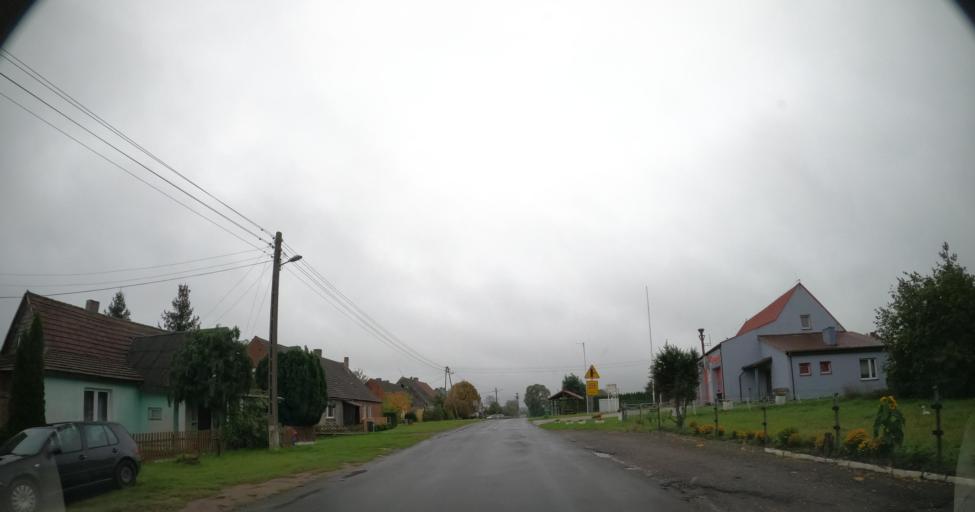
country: PL
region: West Pomeranian Voivodeship
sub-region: Powiat pyrzycki
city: Kozielice
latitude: 53.0472
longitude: 14.7743
